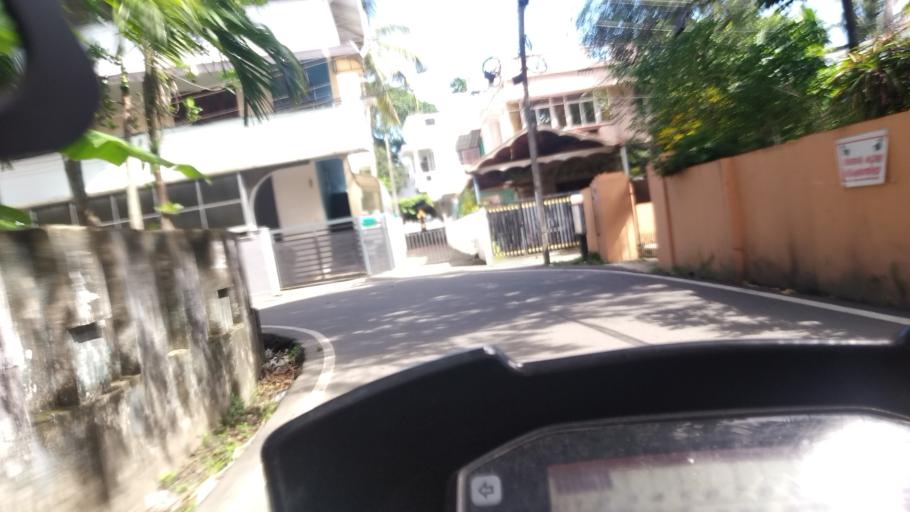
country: IN
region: Kerala
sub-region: Ernakulam
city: Elur
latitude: 10.0260
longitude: 76.2695
